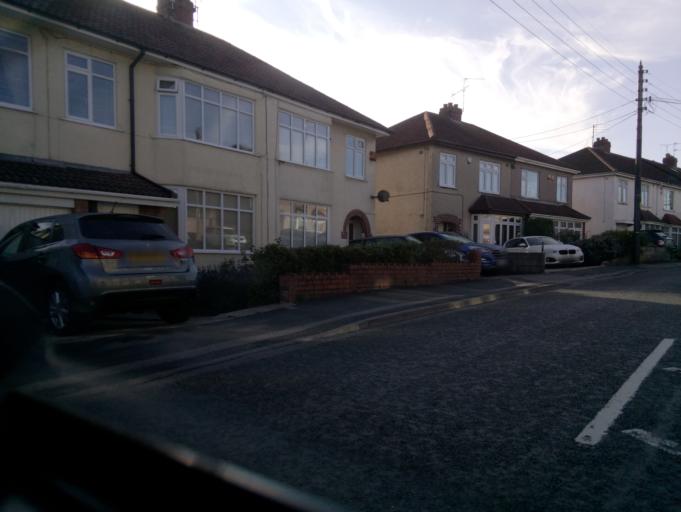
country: GB
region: England
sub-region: South Gloucestershire
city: Mangotsfield
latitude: 51.4781
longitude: -2.4963
